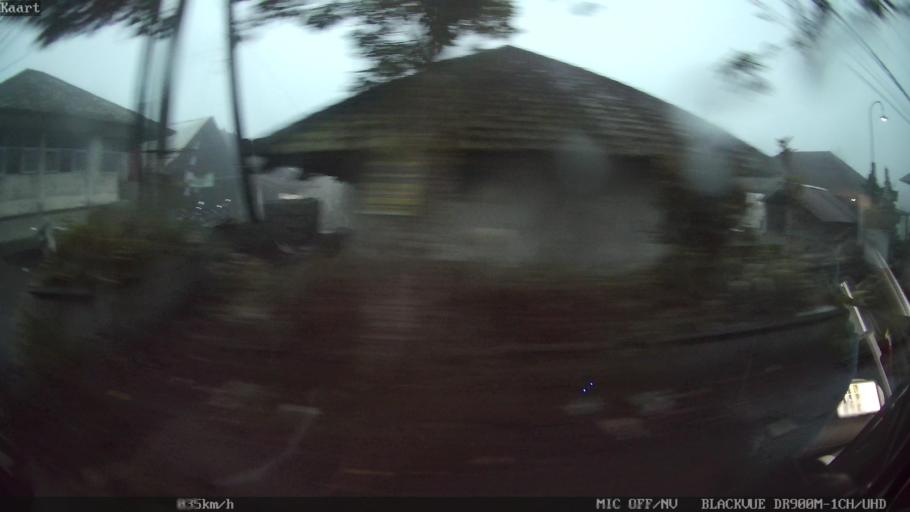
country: ID
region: Bali
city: Banjar Taro Kelod
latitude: -8.3368
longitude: 115.2840
